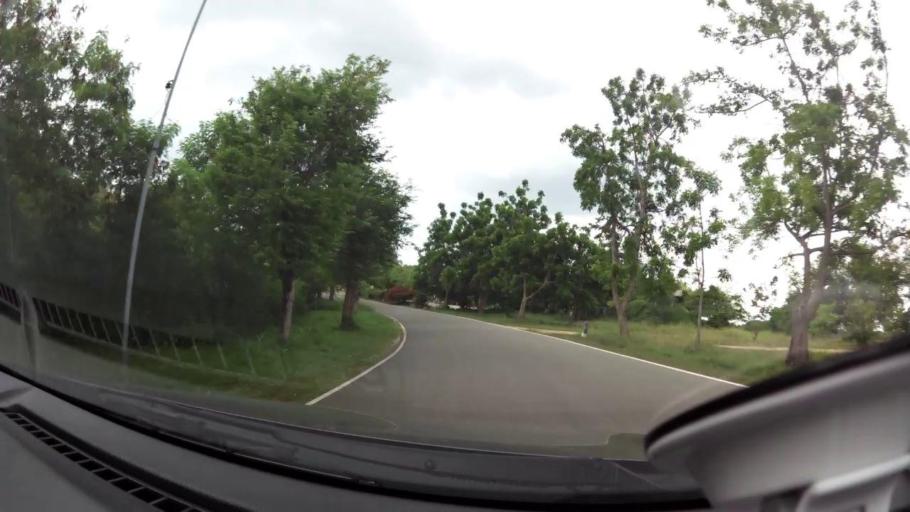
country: TH
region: Phetchaburi
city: Cha-am
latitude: 12.6987
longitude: 99.9587
